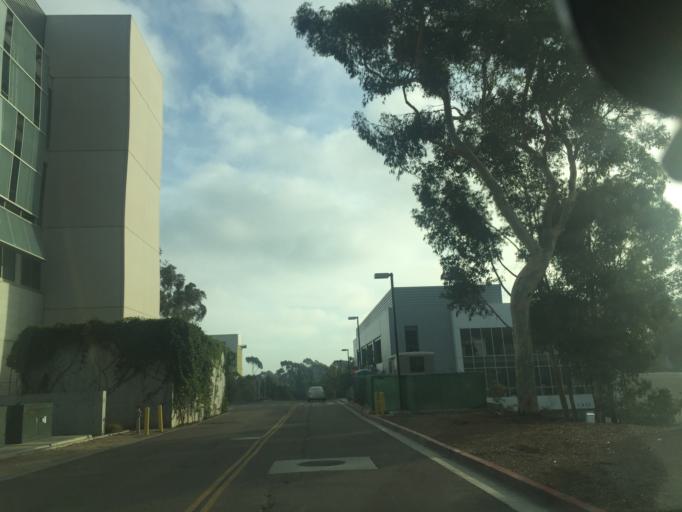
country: US
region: California
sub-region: San Diego County
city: La Jolla
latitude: 32.8743
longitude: -117.2360
